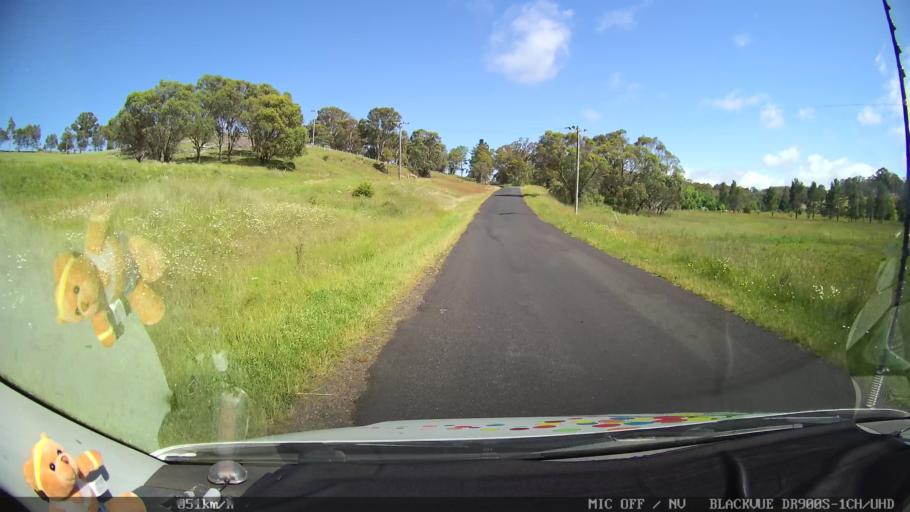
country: AU
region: New South Wales
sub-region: Guyra
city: Guyra
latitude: -30.1118
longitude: 151.6827
